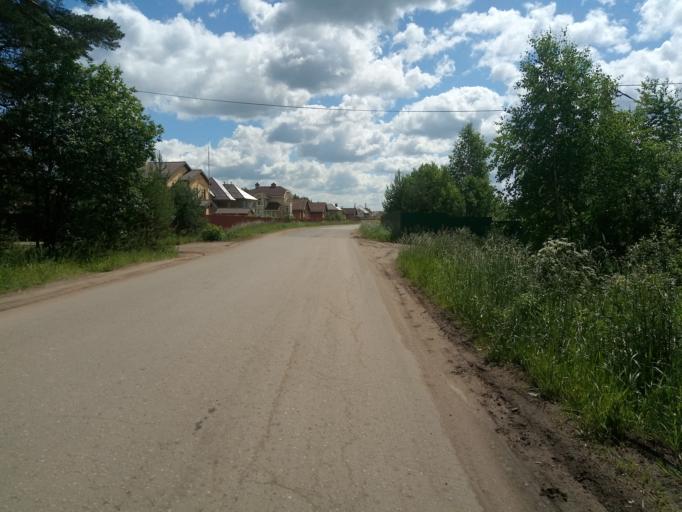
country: RU
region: Jaroslavl
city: Yaroslavl
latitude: 57.6542
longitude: 39.9866
